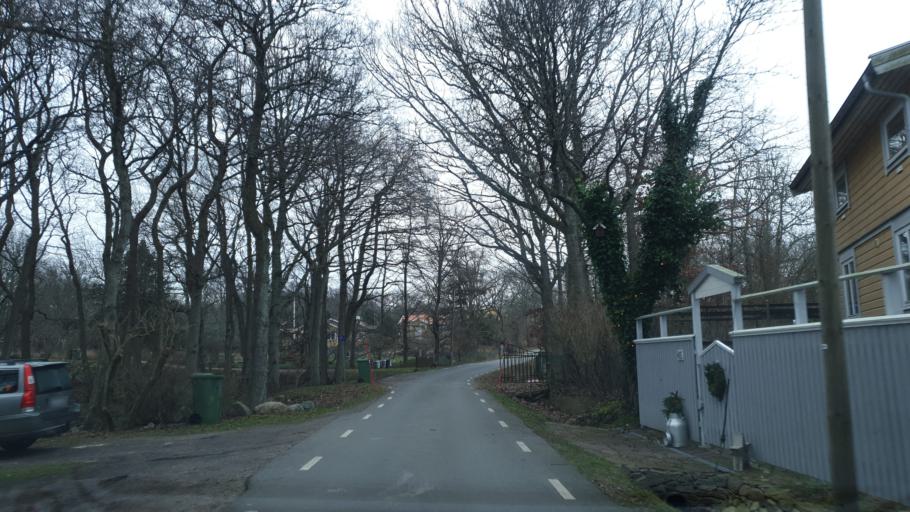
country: SE
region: Blekinge
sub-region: Karlskrona Kommun
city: Karlskrona
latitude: 56.1304
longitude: 15.6197
